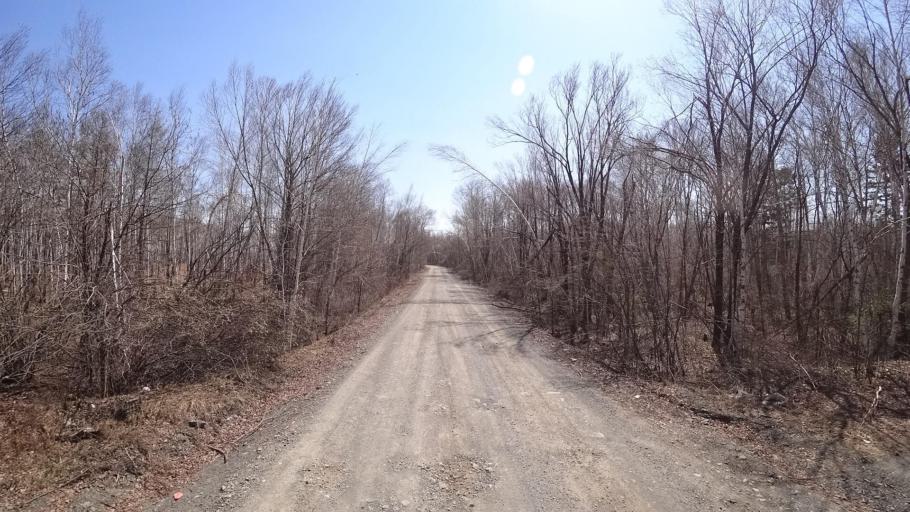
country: RU
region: Khabarovsk Krai
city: Khurba
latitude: 50.4195
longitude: 136.8331
